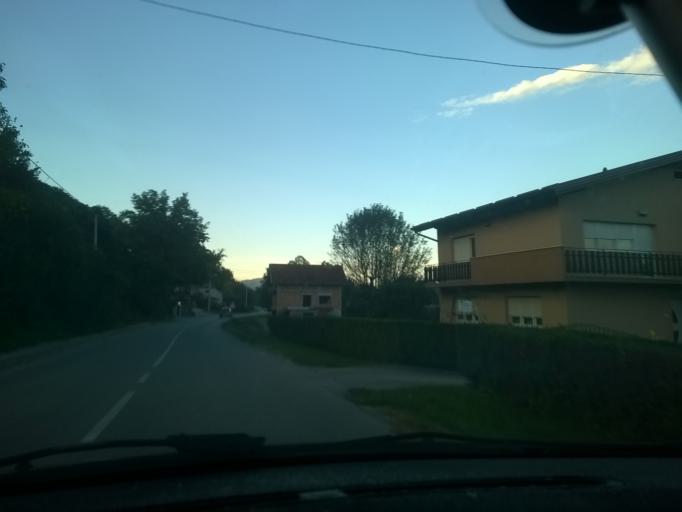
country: HR
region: Krapinsko-Zagorska
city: Zabok
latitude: 46.0438
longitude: 15.9102
